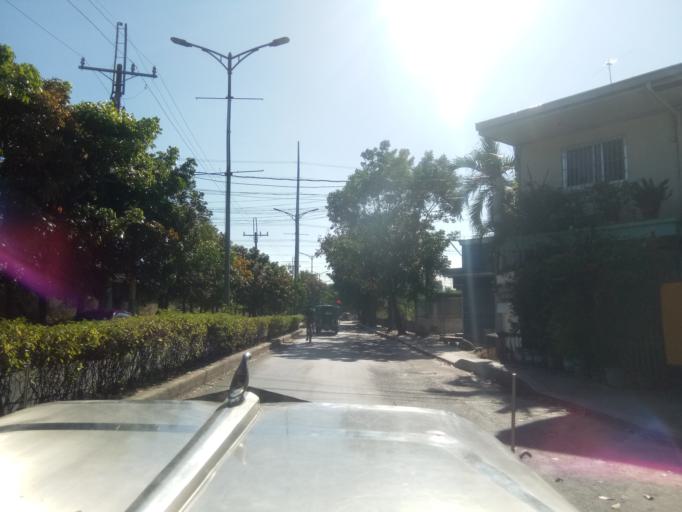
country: PH
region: Calabarzon
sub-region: Province of Cavite
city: Dasmarinas
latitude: 14.3227
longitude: 120.9431
